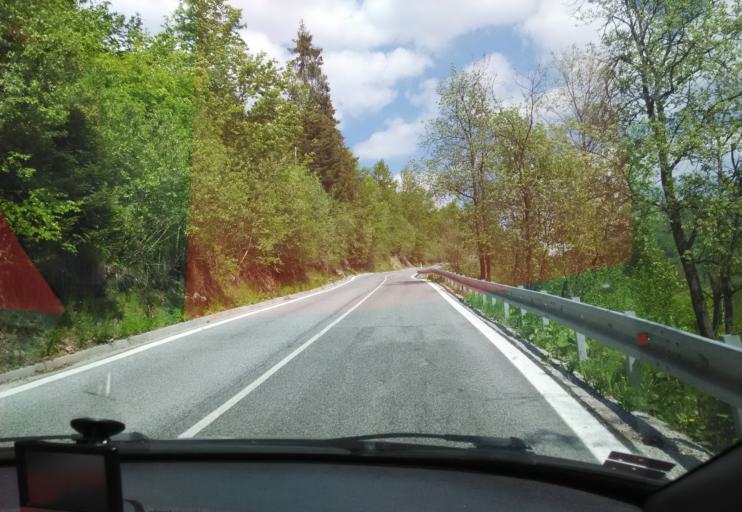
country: SK
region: Kosicky
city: Dobsina
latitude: 48.8433
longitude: 20.4343
